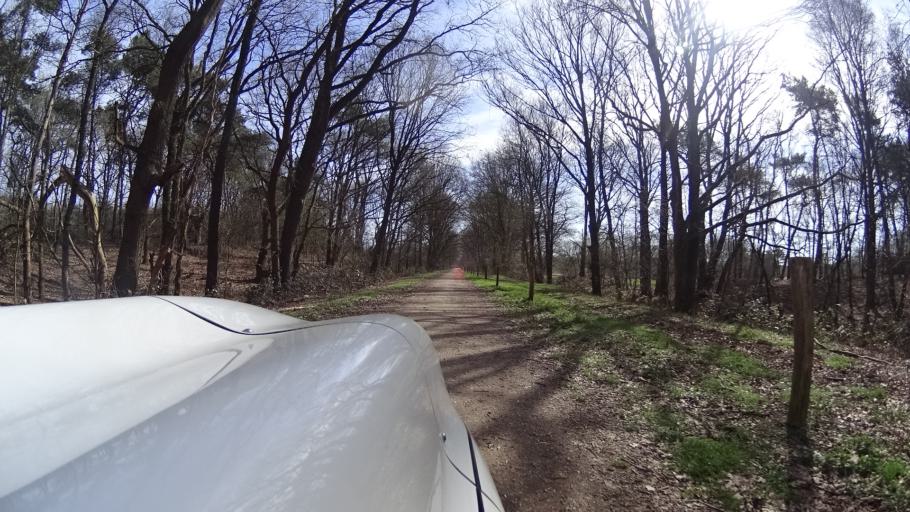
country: NL
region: Limburg
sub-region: Gemeente Gennep
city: Gennep
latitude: 51.6915
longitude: 6.0024
